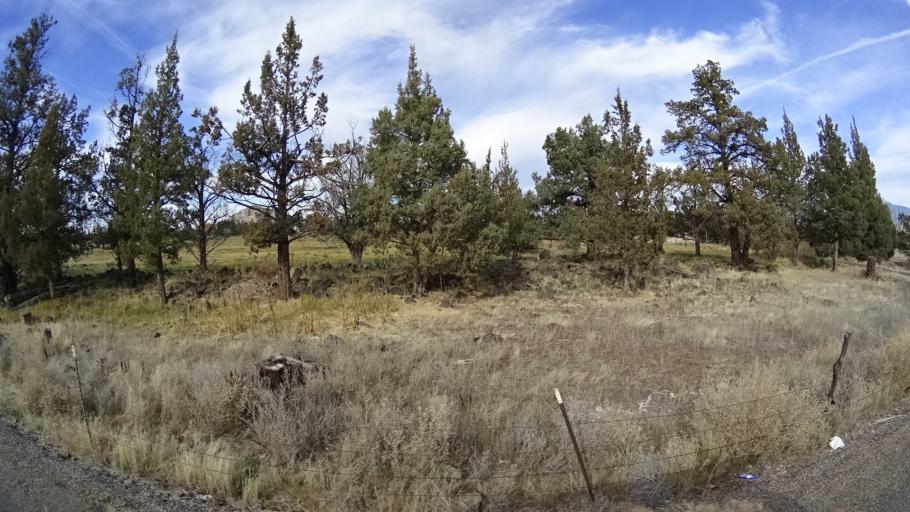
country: US
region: California
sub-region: Siskiyou County
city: Montague
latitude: 41.6384
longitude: -122.4099
